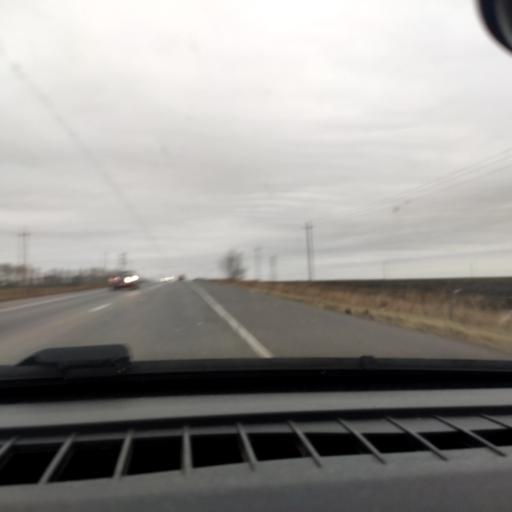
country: RU
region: Voronezj
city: Strelitsa
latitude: 51.5491
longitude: 38.9717
